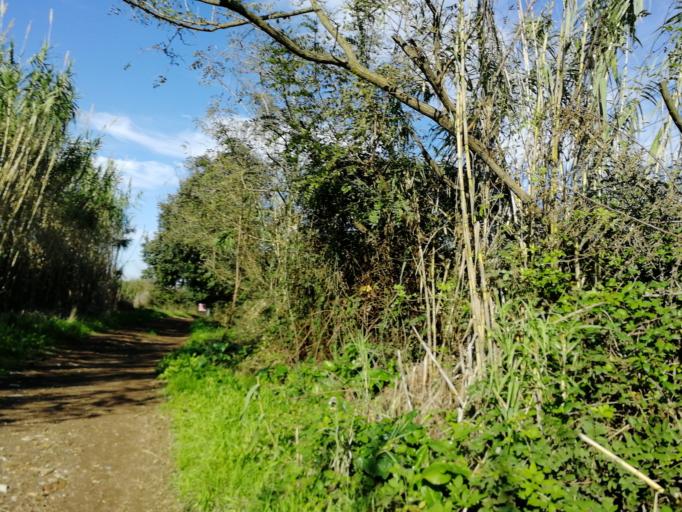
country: IT
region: Latium
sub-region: Citta metropolitana di Roma Capitale
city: Rome
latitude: 41.8570
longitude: 12.5472
